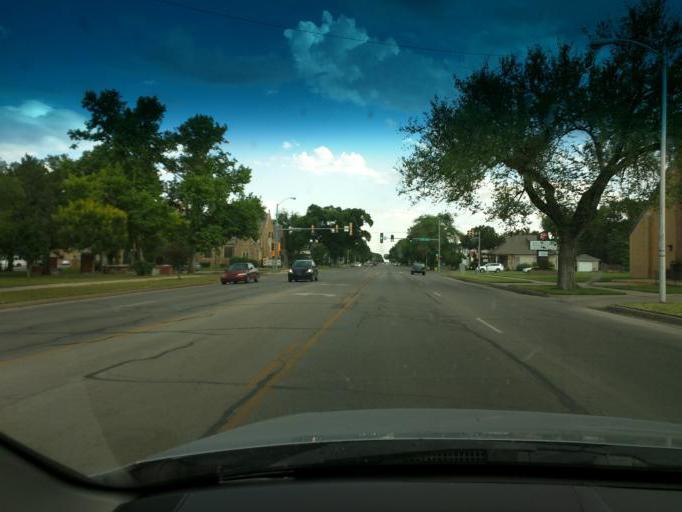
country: US
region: Kansas
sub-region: Reno County
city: Hutchinson
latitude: 38.0726
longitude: -97.9320
